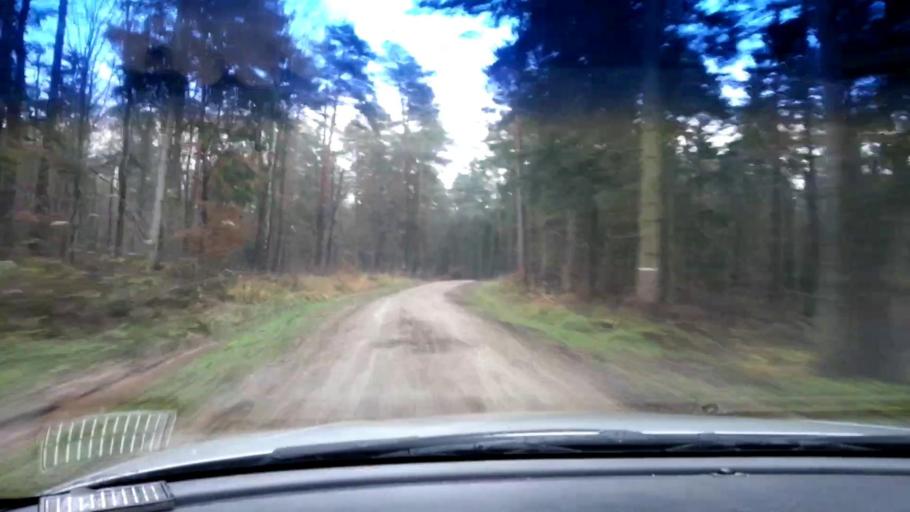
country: DE
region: Bavaria
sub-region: Upper Franconia
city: Gundelsheim
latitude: 49.9479
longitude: 10.9041
